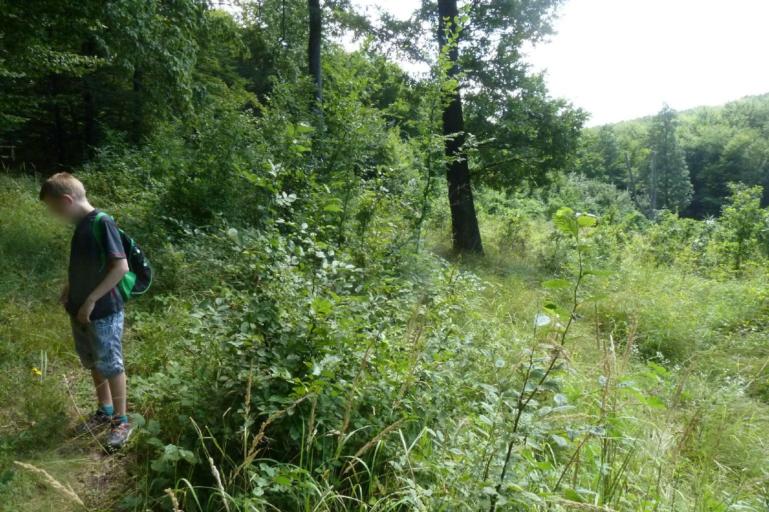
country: HU
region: Pest
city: Szob
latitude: 47.8981
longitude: 18.9040
